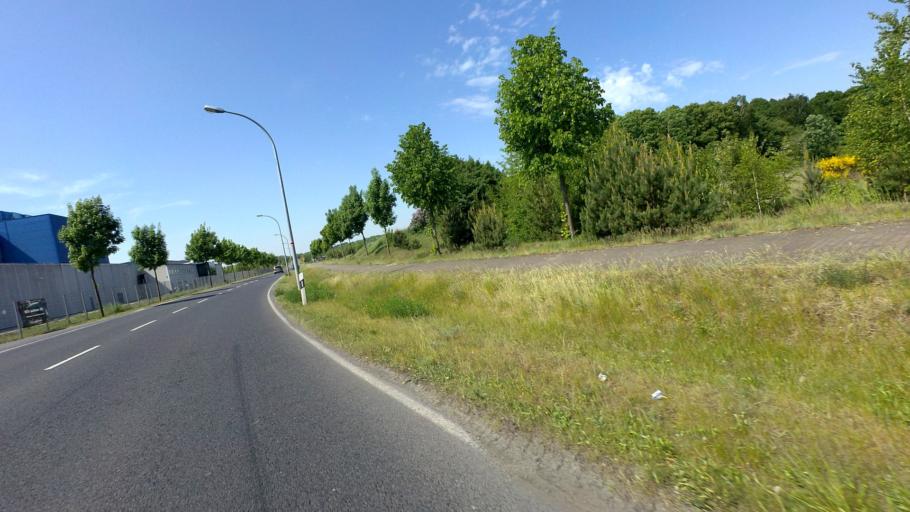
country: DE
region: Brandenburg
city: Leegebruch
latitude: 52.7220
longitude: 13.2272
